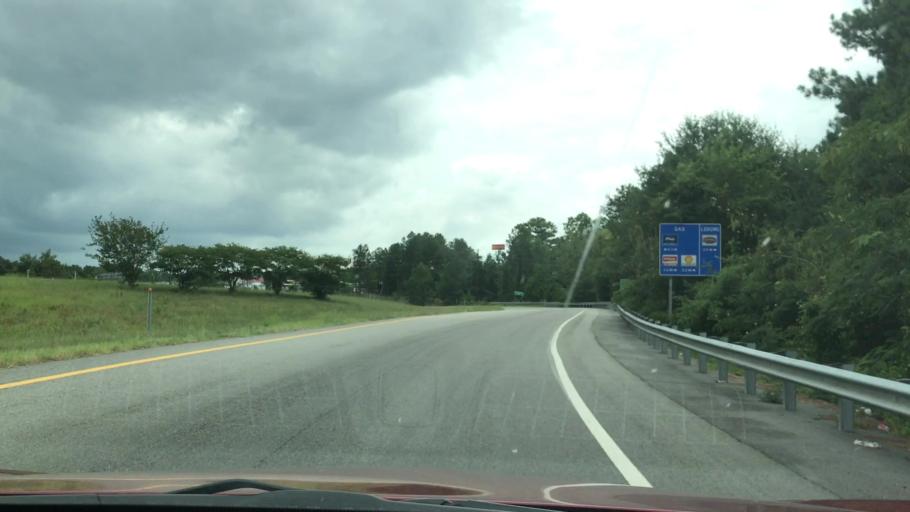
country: US
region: South Carolina
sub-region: Lexington County
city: Cayce
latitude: 33.9334
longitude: -81.0790
